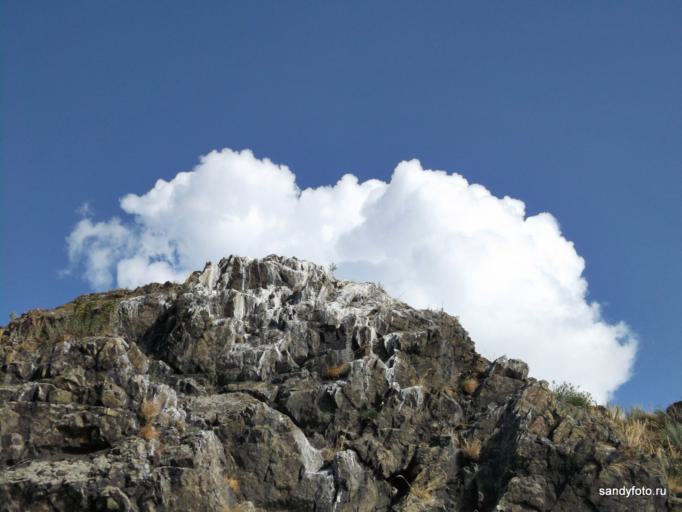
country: RU
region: Chelyabinsk
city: Troitsk
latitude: 54.0762
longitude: 61.5758
